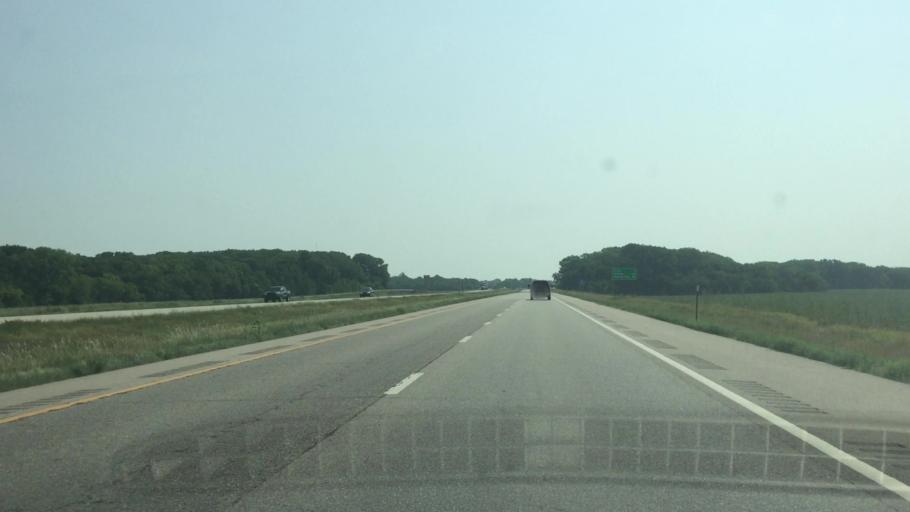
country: US
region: Kansas
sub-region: Lyon County
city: Emporia
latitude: 38.4109
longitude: -96.1253
